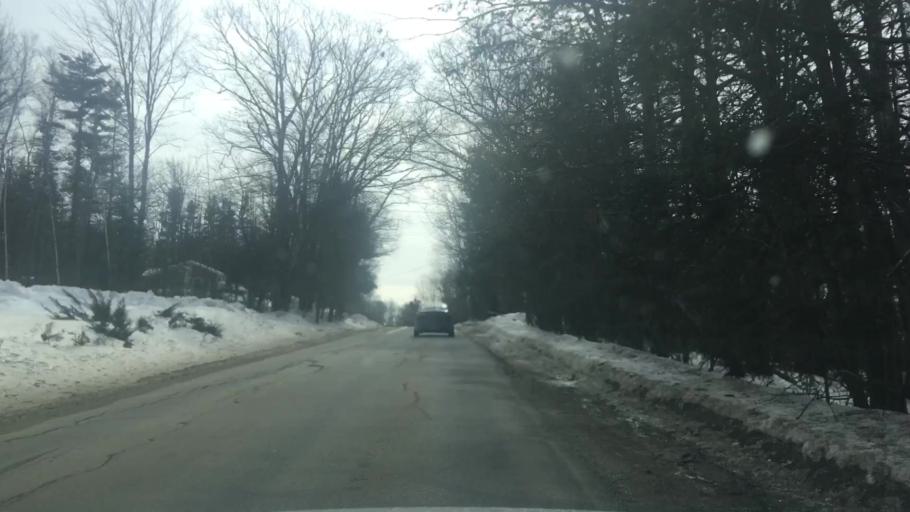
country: US
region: Maine
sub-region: Hancock County
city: Orland
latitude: 44.5889
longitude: -68.7257
